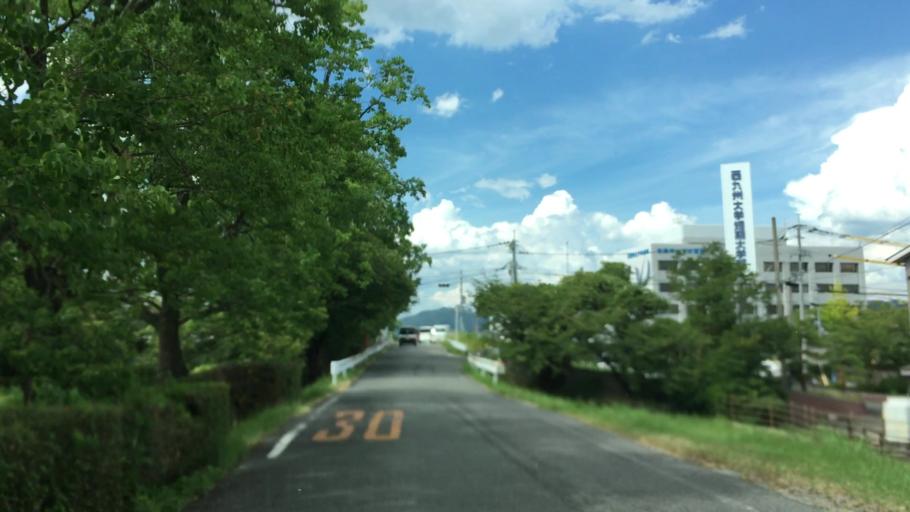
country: JP
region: Saga Prefecture
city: Saga-shi
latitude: 33.2721
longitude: 130.2824
